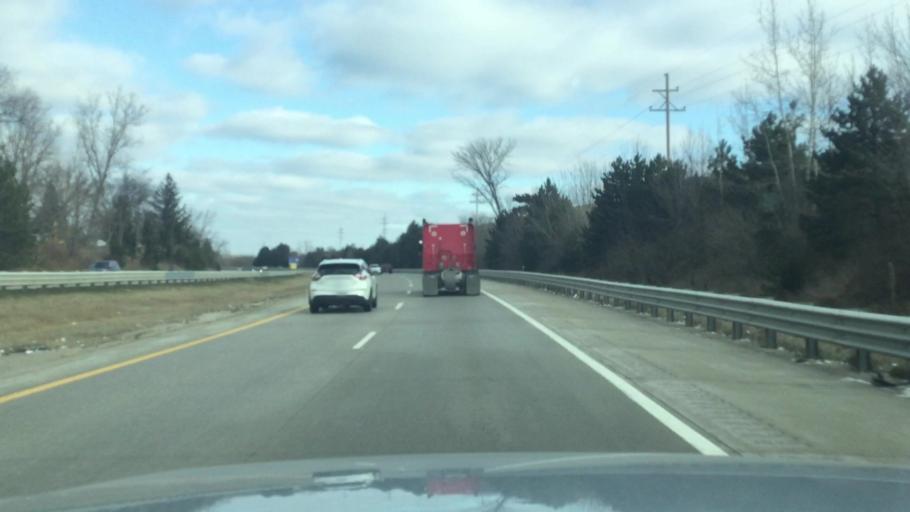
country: US
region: Michigan
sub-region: Genesee County
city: Lake Fenton
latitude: 42.9030
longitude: -83.7298
